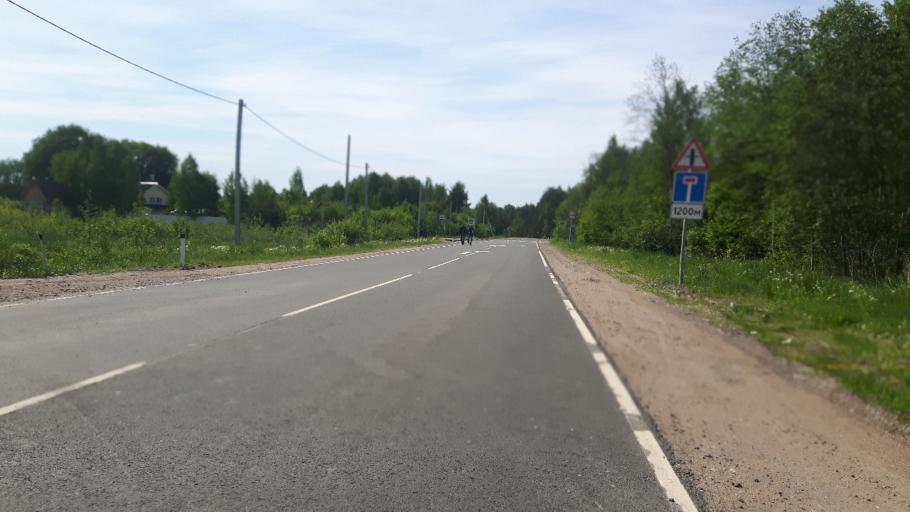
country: RU
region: Leningrad
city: Vistino
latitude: 59.6743
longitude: 28.4504
